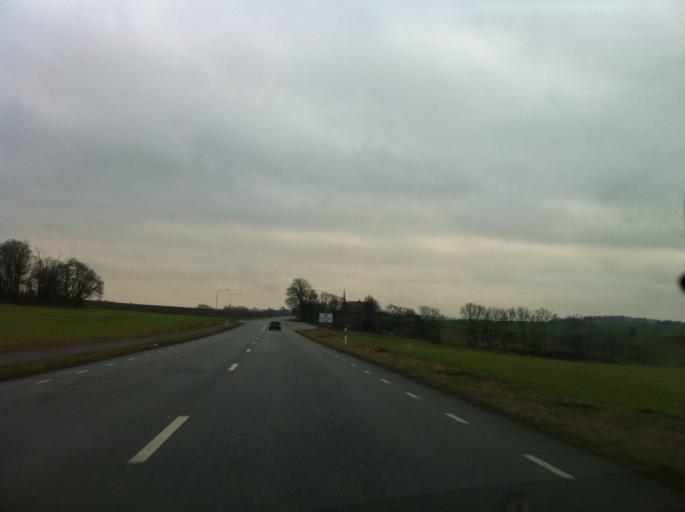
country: SE
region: Skane
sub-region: Helsingborg
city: Glumslov
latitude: 55.9384
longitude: 12.8155
